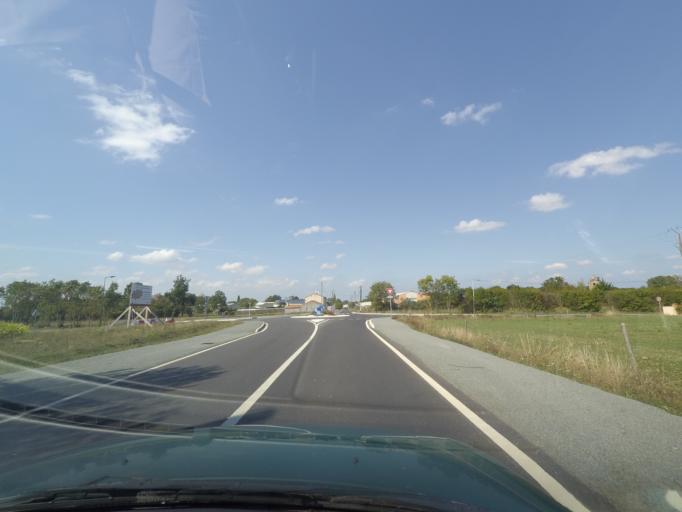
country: FR
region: Pays de la Loire
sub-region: Departement de la Loire-Atlantique
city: Saint-Lumine-de-Coutais
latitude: 47.0489
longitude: -1.7223
